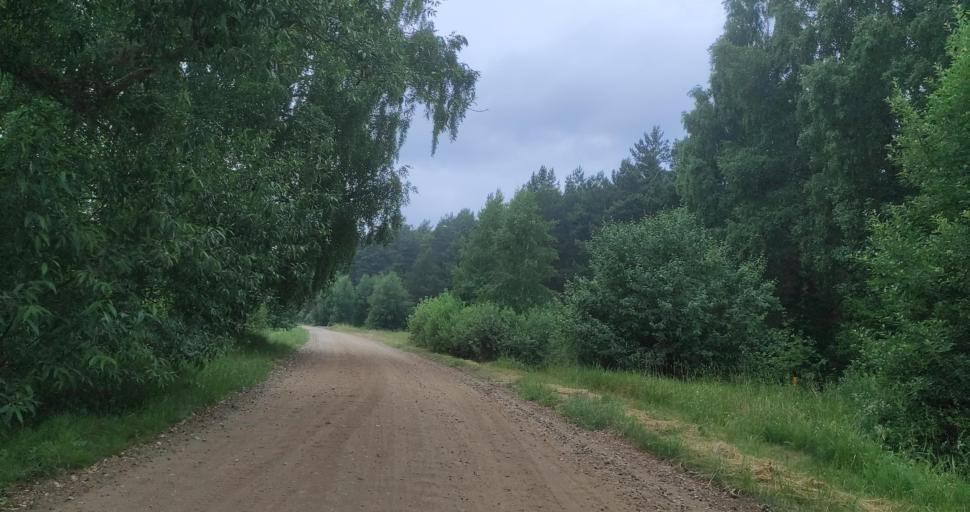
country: LV
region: Pavilostas
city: Pavilosta
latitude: 56.8855
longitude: 21.2061
